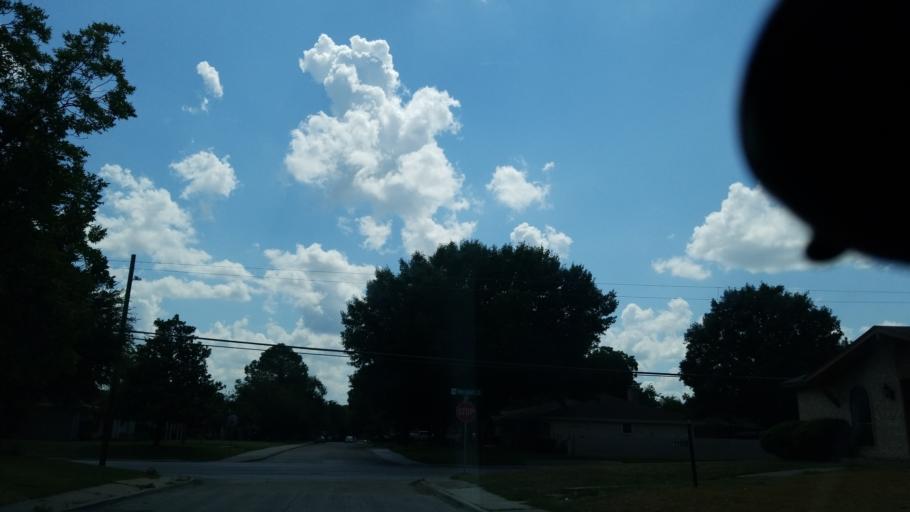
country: US
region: Texas
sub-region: Dallas County
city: Grand Prairie
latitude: 32.7209
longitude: -96.9985
